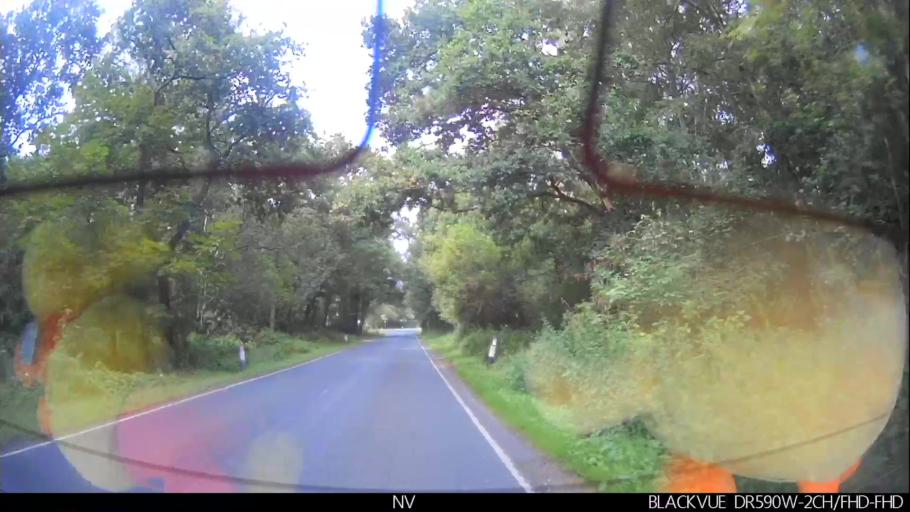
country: GB
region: England
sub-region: North Yorkshire
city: Strensall
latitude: 54.0360
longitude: -1.0245
